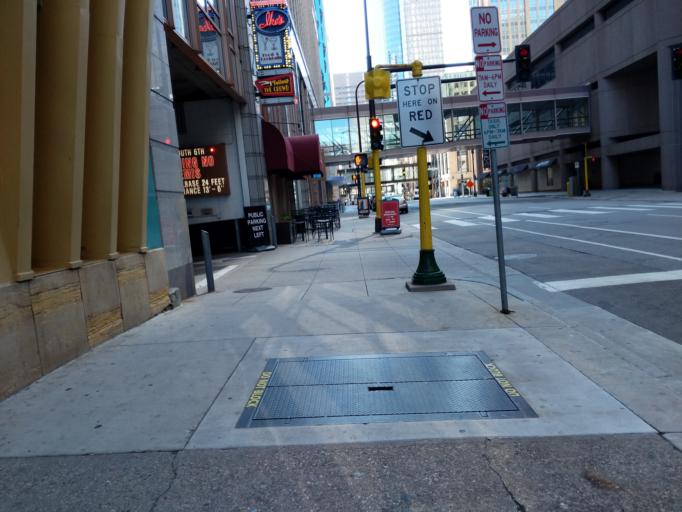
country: US
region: Minnesota
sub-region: Hennepin County
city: Minneapolis
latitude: 44.9787
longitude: -93.2723
